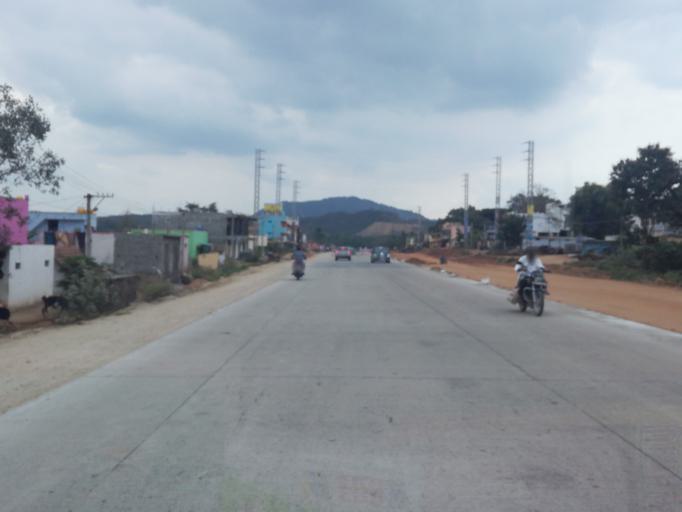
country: IN
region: Andhra Pradesh
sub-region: Chittoor
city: Ramapuram
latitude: 13.1023
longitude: 79.1247
